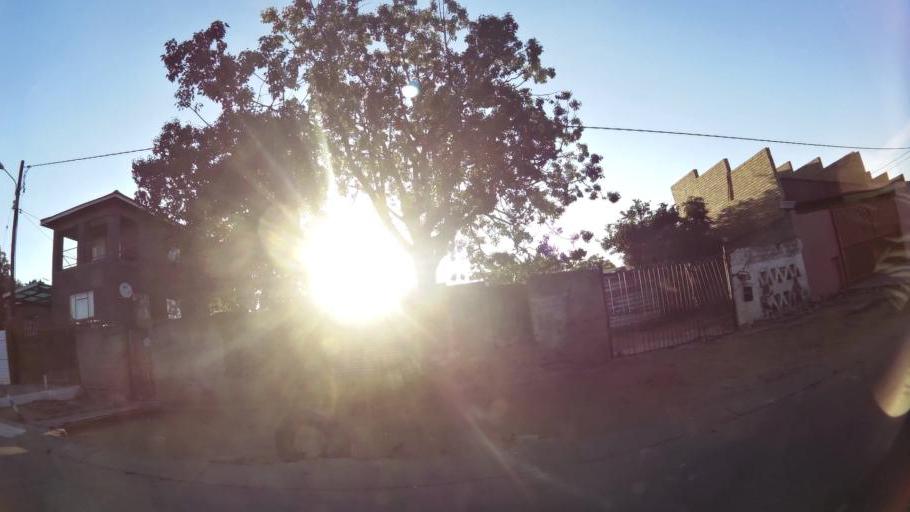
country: ZA
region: North-West
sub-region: Bojanala Platinum District Municipality
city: Rustenburg
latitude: -25.6327
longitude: 27.2064
